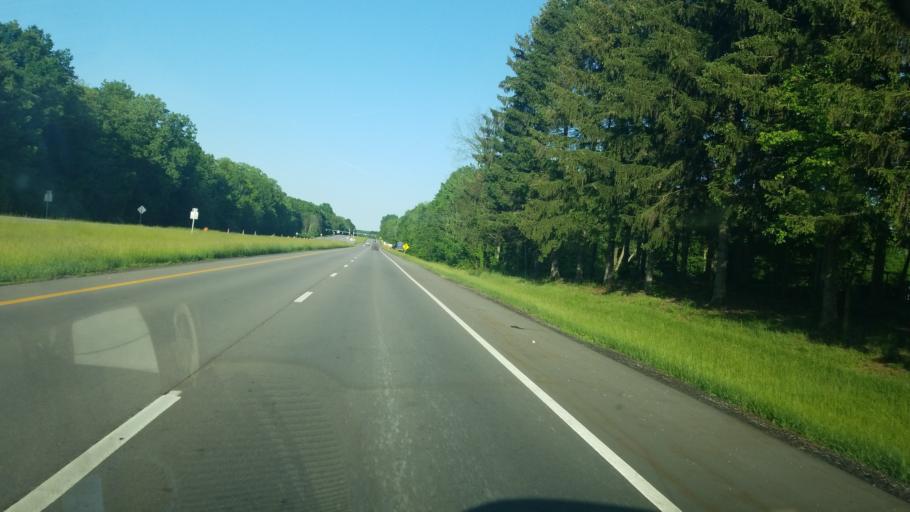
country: US
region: Ohio
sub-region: Portage County
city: Kent
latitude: 41.1344
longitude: -81.3514
